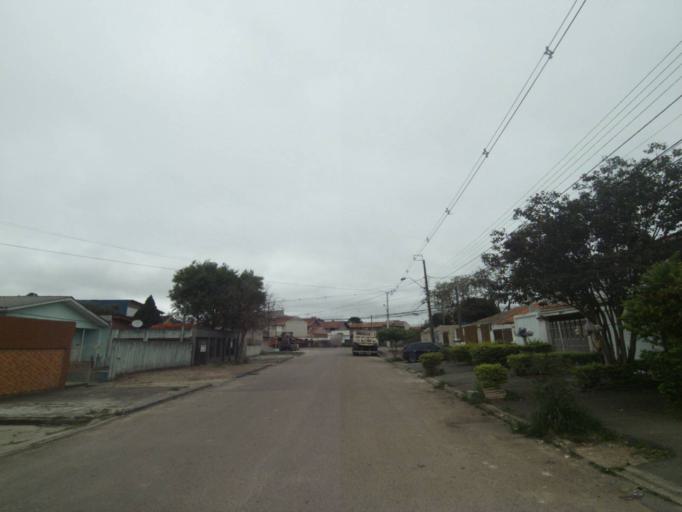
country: BR
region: Parana
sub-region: Curitiba
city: Curitiba
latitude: -25.4657
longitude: -49.2696
